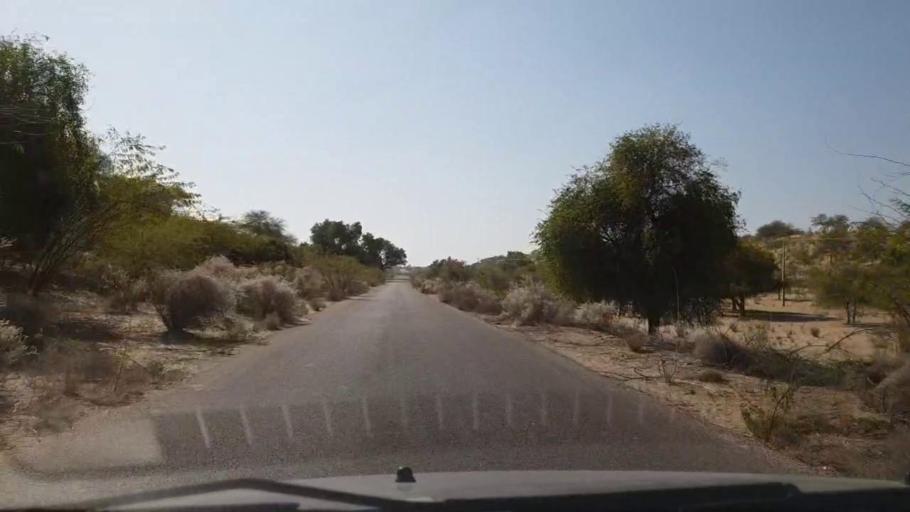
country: PK
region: Sindh
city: Diplo
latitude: 24.5484
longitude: 69.6534
